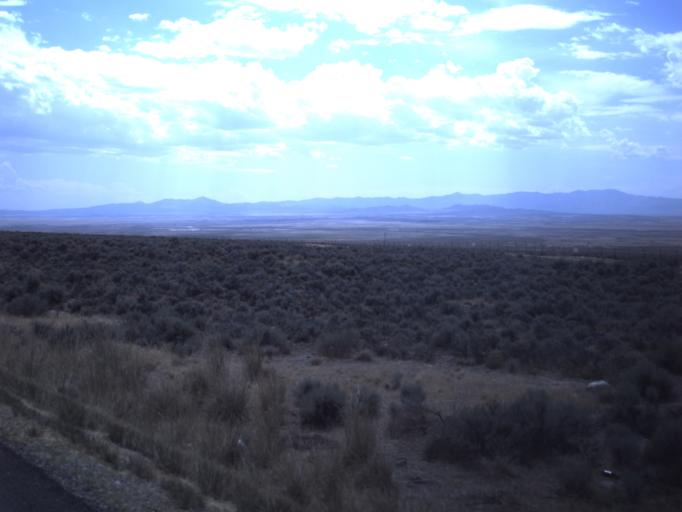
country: US
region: Utah
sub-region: Tooele County
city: Tooele
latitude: 40.3042
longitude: -112.2783
